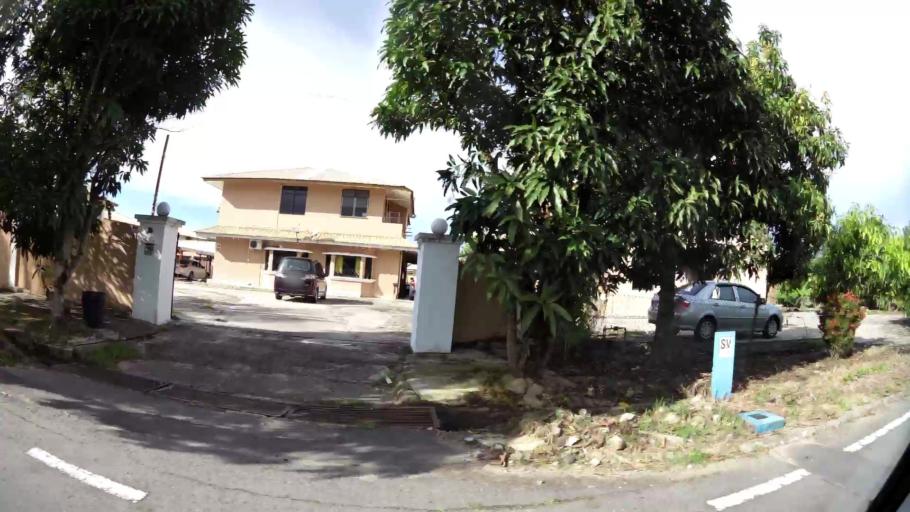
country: BN
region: Brunei and Muara
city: Bandar Seri Begawan
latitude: 4.9716
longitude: 115.0265
